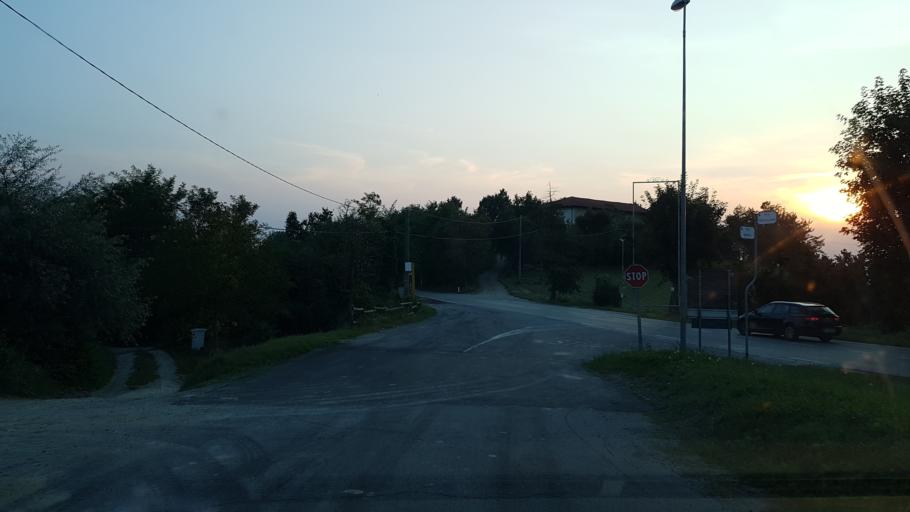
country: IT
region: Piedmont
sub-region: Provincia di Cuneo
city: Novello
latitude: 44.5860
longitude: 7.9226
